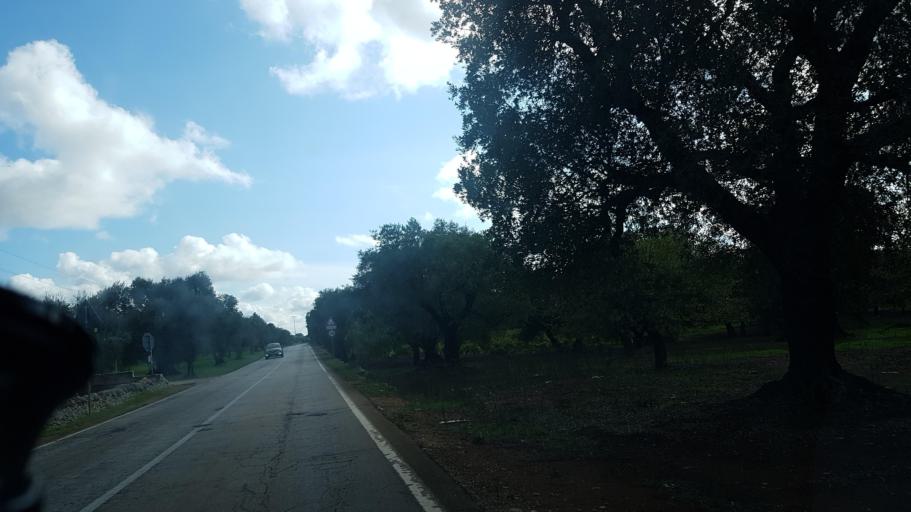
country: IT
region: Apulia
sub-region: Provincia di Brindisi
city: San Michele Salentino
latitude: 40.6504
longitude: 17.6059
